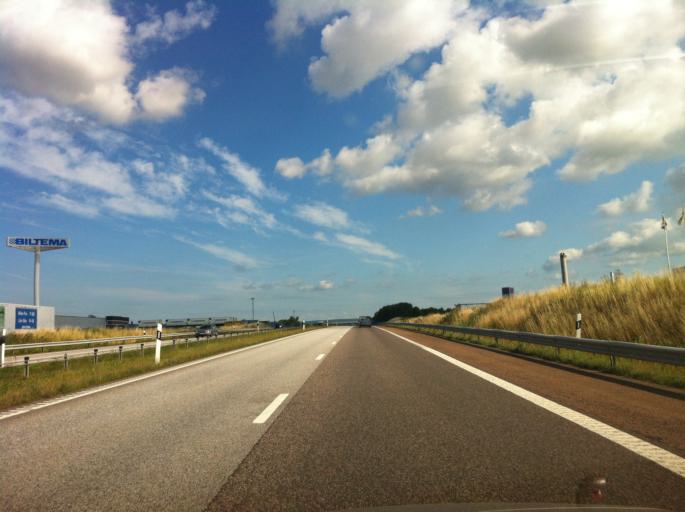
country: SE
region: Skane
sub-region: Angelholms Kommun
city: AEngelholm
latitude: 56.2422
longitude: 12.8990
